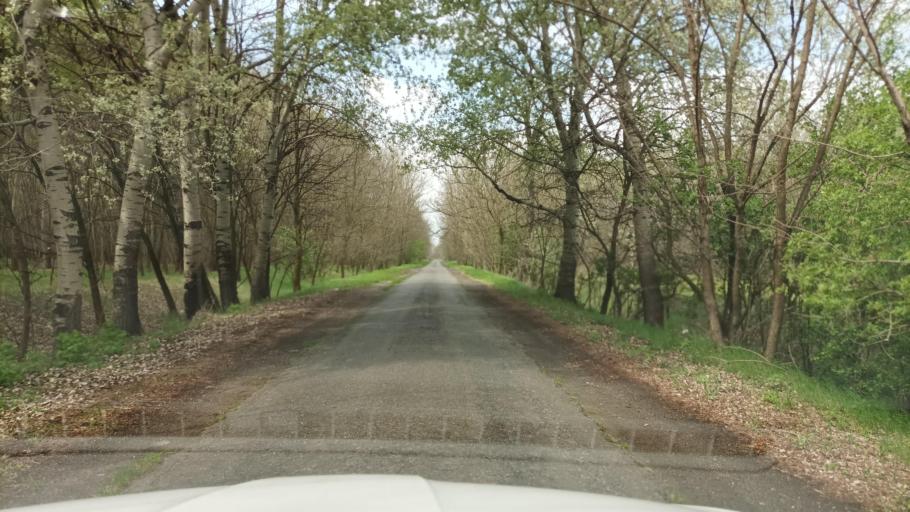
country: HU
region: Pest
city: Kocser
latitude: 47.0501
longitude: 19.9028
